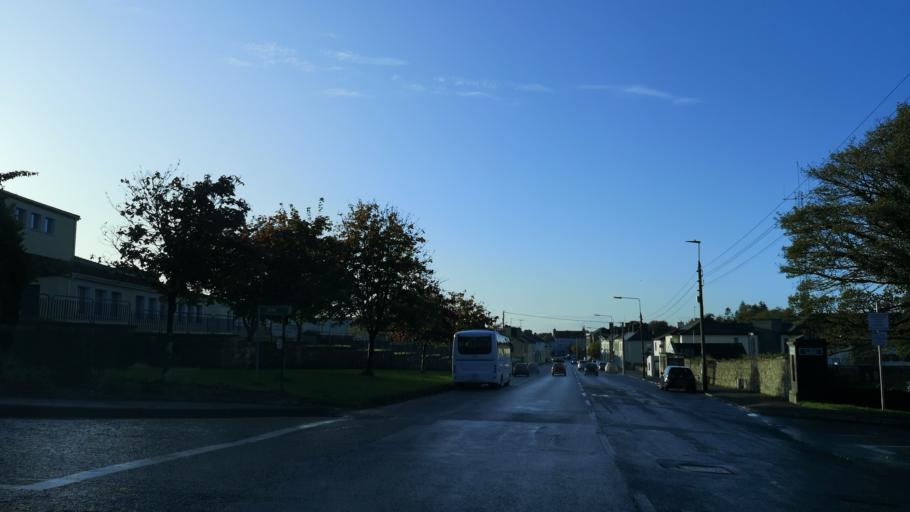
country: IE
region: Connaught
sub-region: Roscommon
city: Castlerea
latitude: 53.7660
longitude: -8.4827
